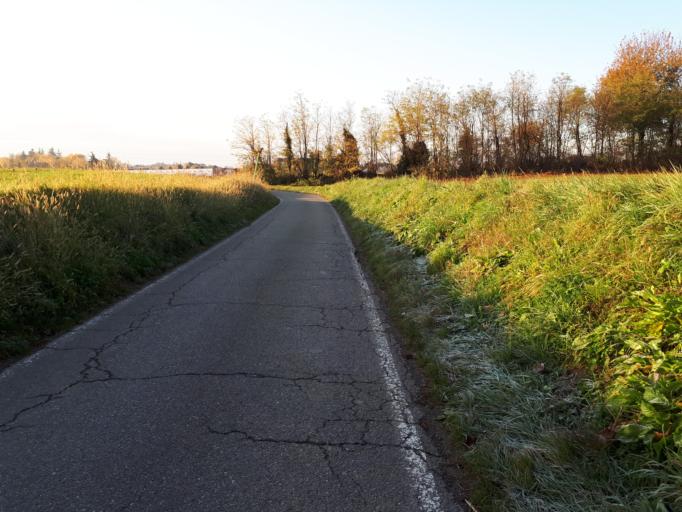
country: IT
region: Lombardy
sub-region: Provincia di Lecco
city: Quattro Strade
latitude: 45.6870
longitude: 9.3785
